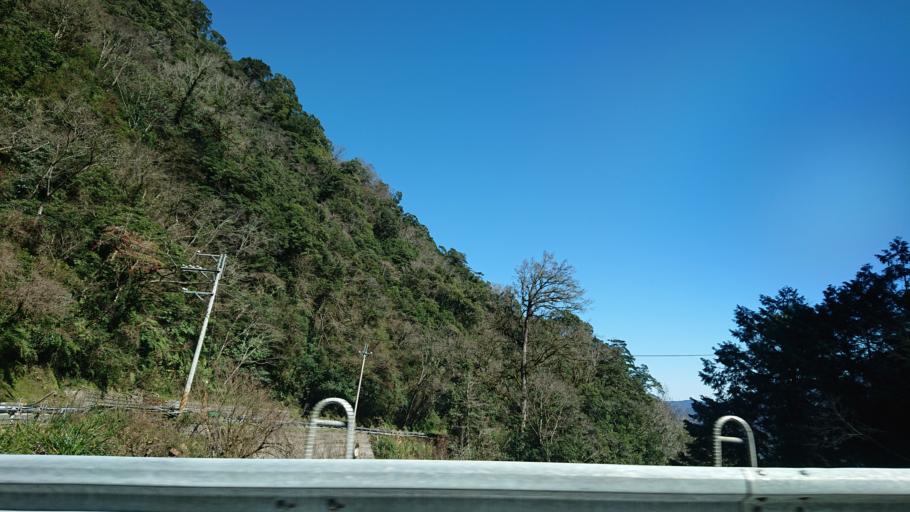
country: TW
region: Taiwan
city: Daxi
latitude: 24.4060
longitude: 121.3565
